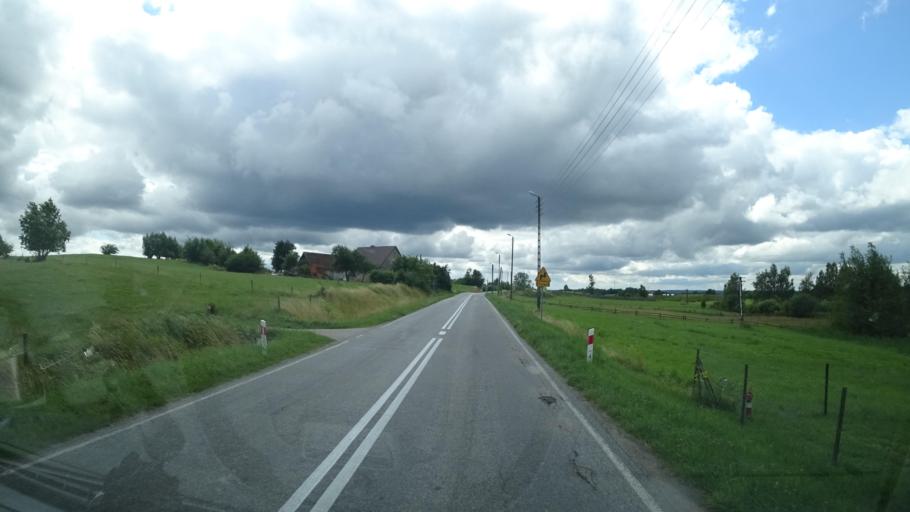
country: PL
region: Warmian-Masurian Voivodeship
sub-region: Powiat goldapski
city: Goldap
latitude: 54.2238
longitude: 22.2343
